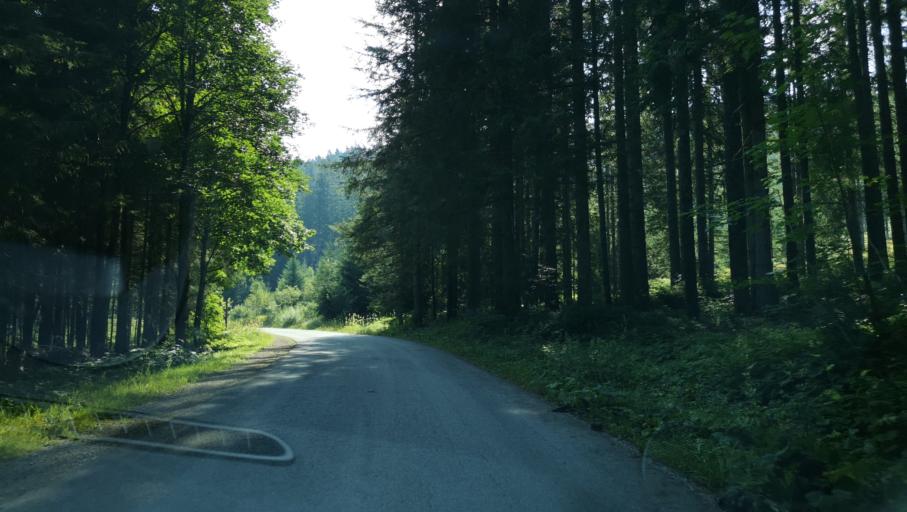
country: AT
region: Styria
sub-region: Politischer Bezirk Liezen
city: Trieben
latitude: 47.5254
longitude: 14.4697
